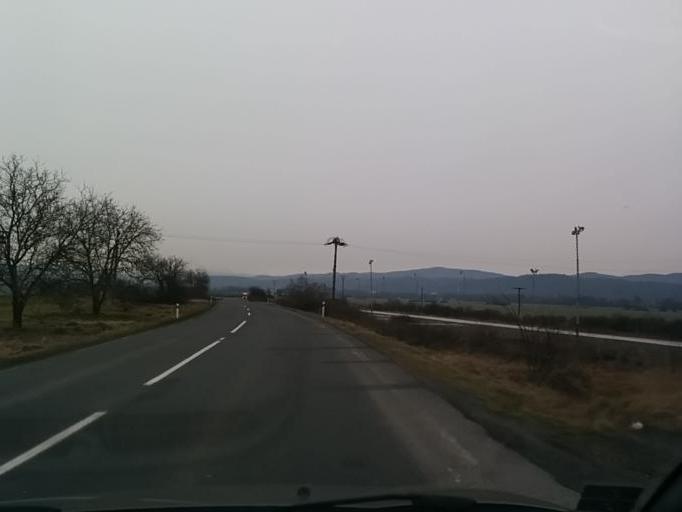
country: SK
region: Banskobystricky
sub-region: Okres Banska Bystrica
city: Zvolen
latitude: 48.6431
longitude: 19.1414
